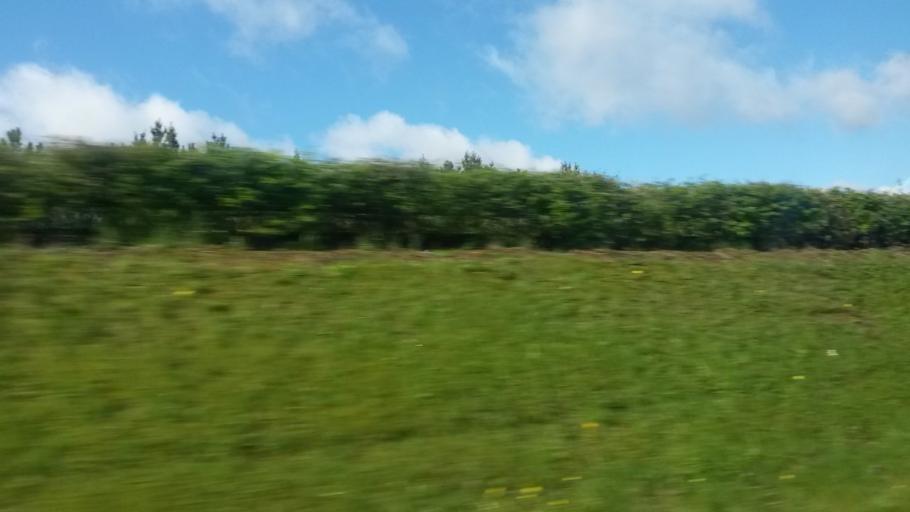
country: IE
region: Munster
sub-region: County Cork
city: Passage West
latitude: 51.9059
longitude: -8.3922
